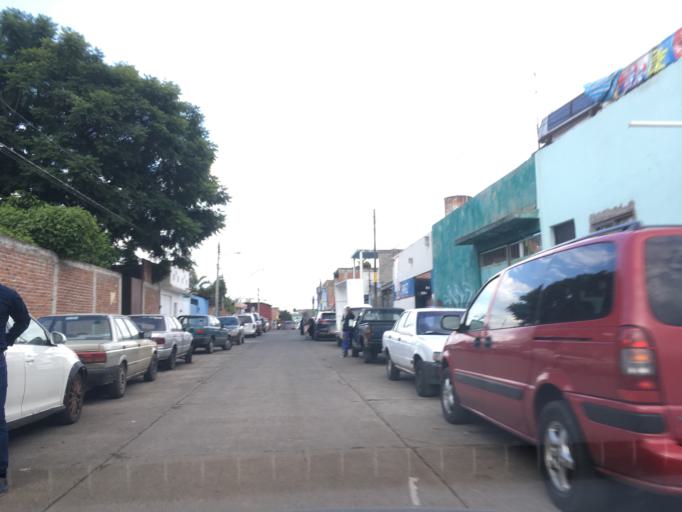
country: MX
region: Michoacan
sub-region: Morelia
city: San Antonio
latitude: 19.6920
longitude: -101.2341
